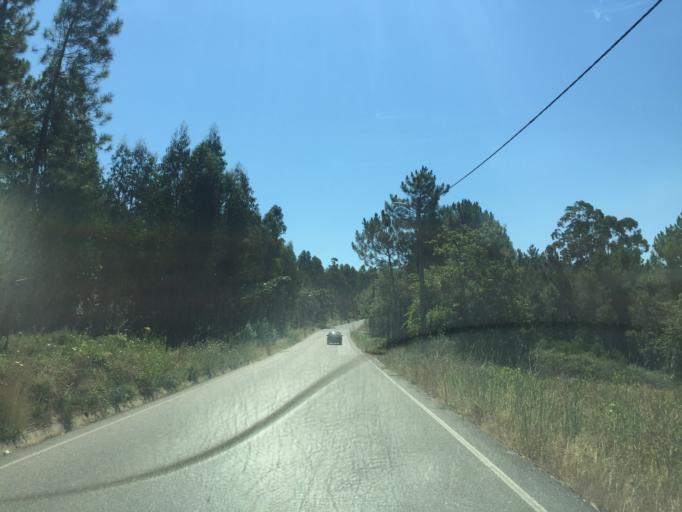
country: PT
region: Santarem
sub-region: Ferreira do Zezere
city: Ferreira do Zezere
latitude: 39.6048
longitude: -8.3079
